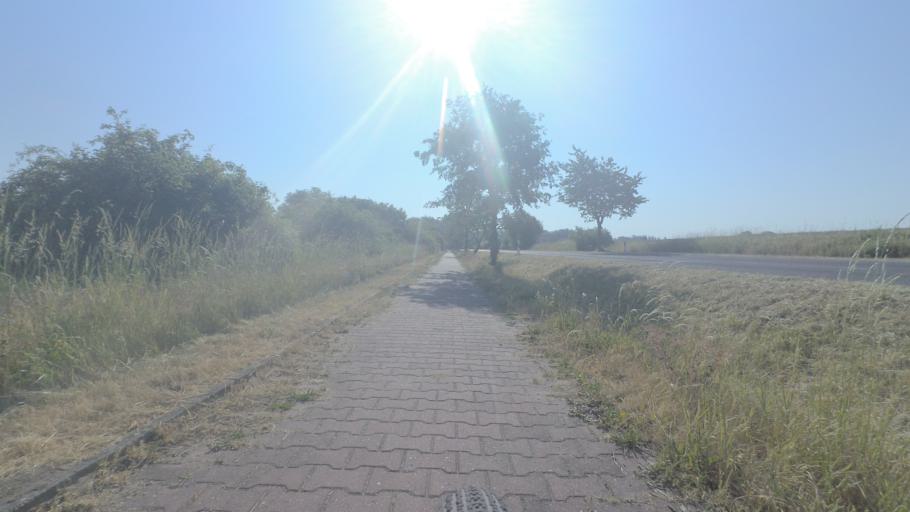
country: DE
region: Saxony-Anhalt
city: Osternienburg
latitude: 51.7921
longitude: 12.0433
